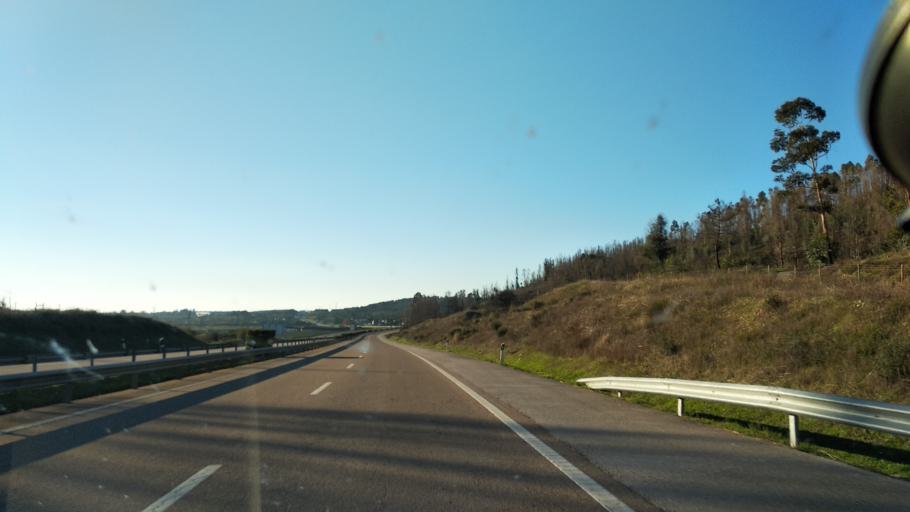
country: PT
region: Santarem
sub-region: Abrantes
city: Tramagal
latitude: 39.4848
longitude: -8.2518
